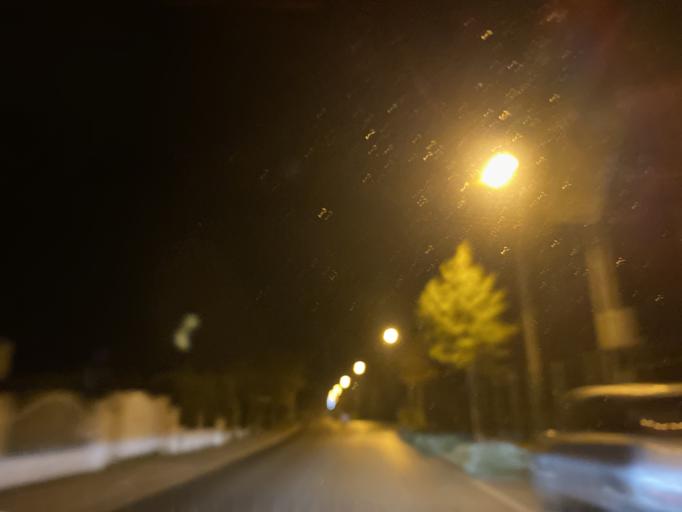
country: FR
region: Auvergne
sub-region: Departement de l'Allier
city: Abrest
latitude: 46.1034
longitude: 3.4405
